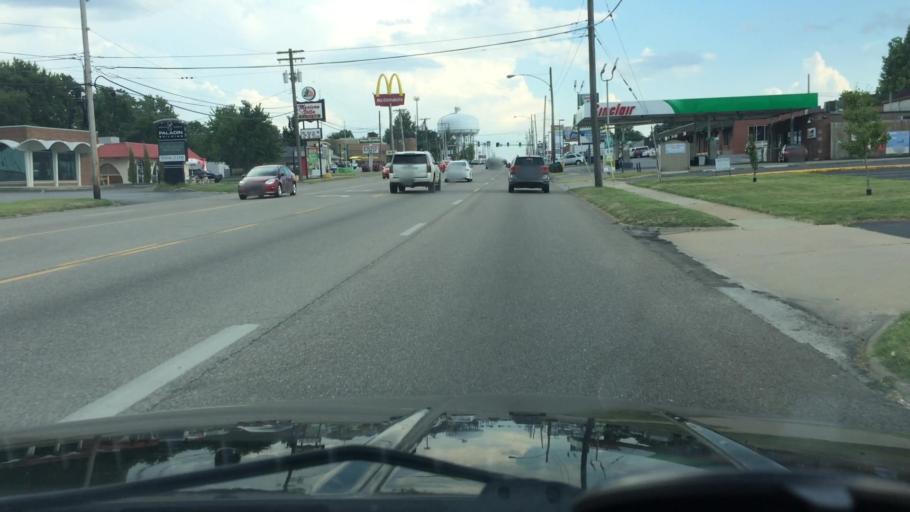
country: US
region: Missouri
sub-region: Greene County
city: Springfield
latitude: 37.2060
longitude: -93.2620
